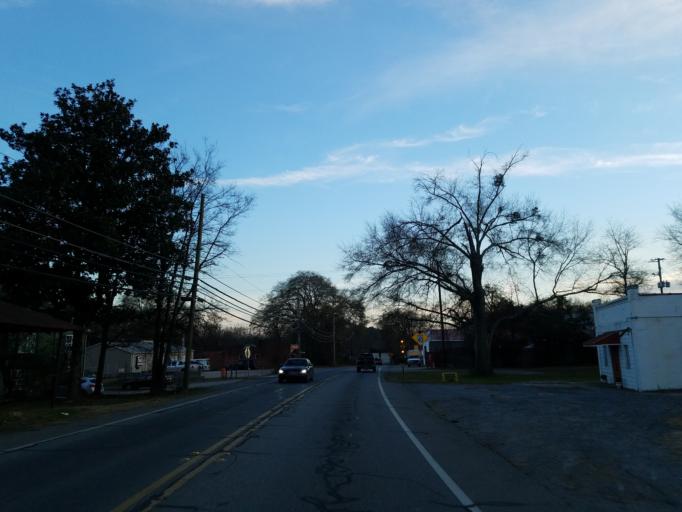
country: US
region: Georgia
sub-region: Bartow County
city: Cartersville
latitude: 34.1844
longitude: -84.8163
